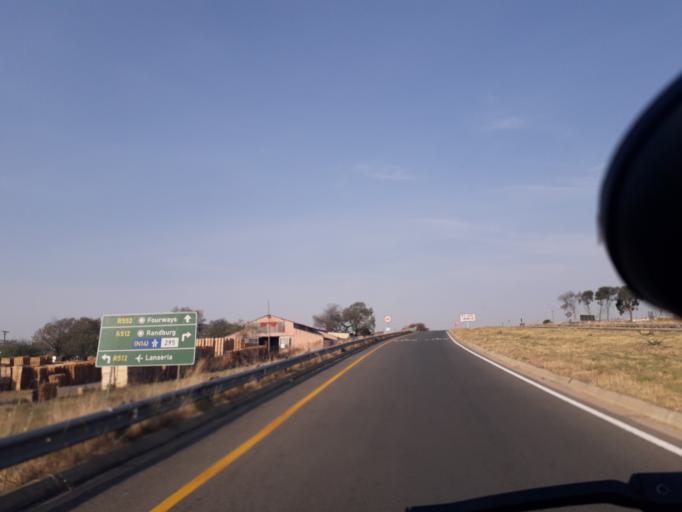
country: ZA
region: Gauteng
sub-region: City of Johannesburg Metropolitan Municipality
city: Diepsloot
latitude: -25.9691
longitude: 27.9190
